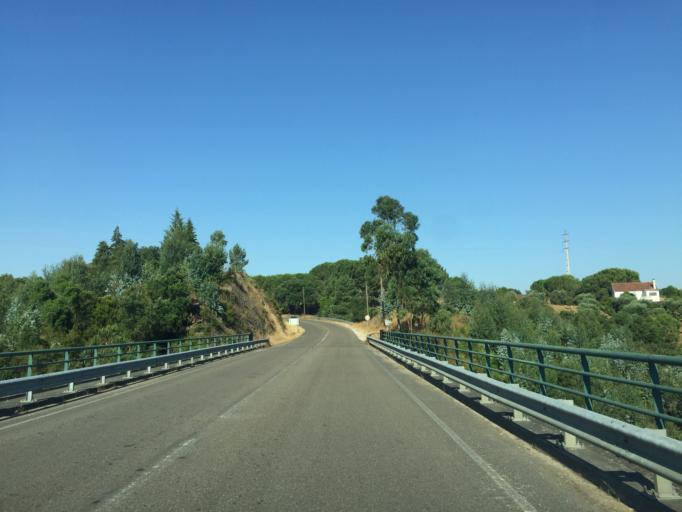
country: PT
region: Santarem
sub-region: Tomar
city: Tomar
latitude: 39.5918
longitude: -8.3465
